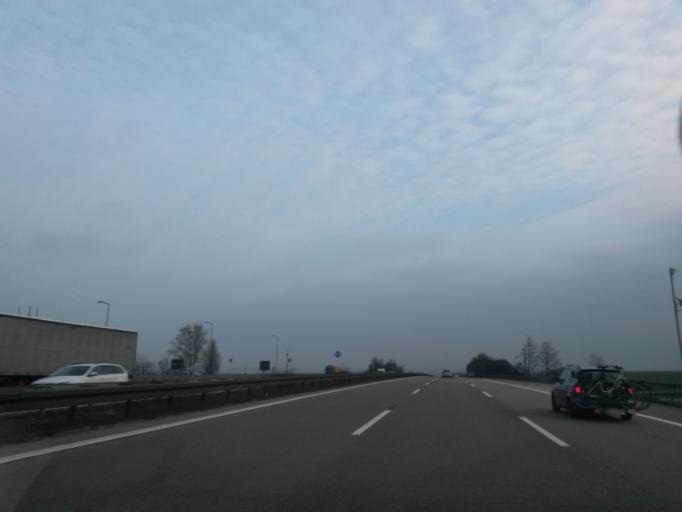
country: DE
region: Bavaria
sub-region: Upper Bavaria
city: Stammham
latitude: 48.8366
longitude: 11.4701
